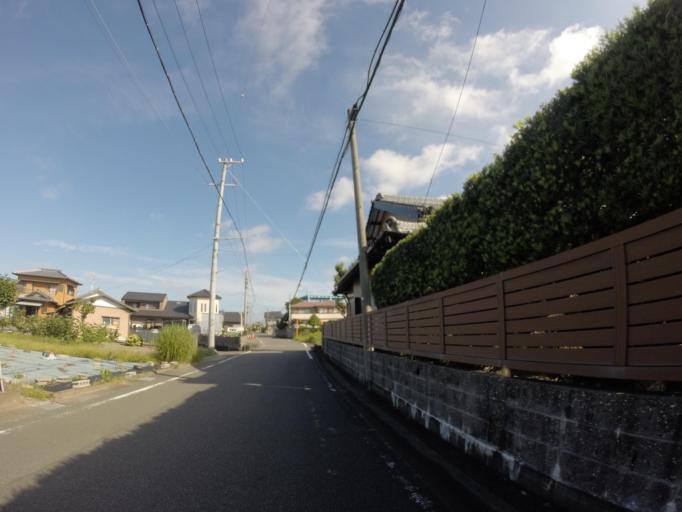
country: JP
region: Shizuoka
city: Fujieda
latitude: 34.7865
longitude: 138.2829
